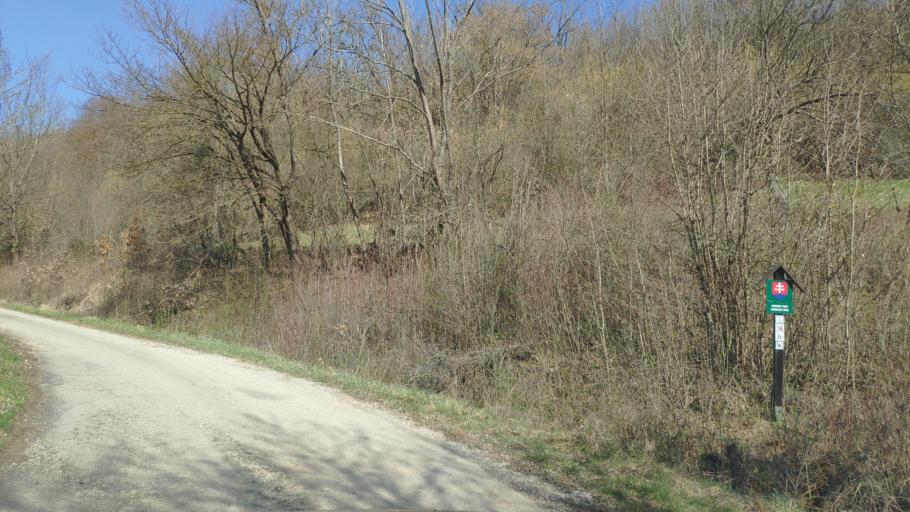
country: SK
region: Kosicky
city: Roznava
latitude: 48.5553
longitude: 20.4154
